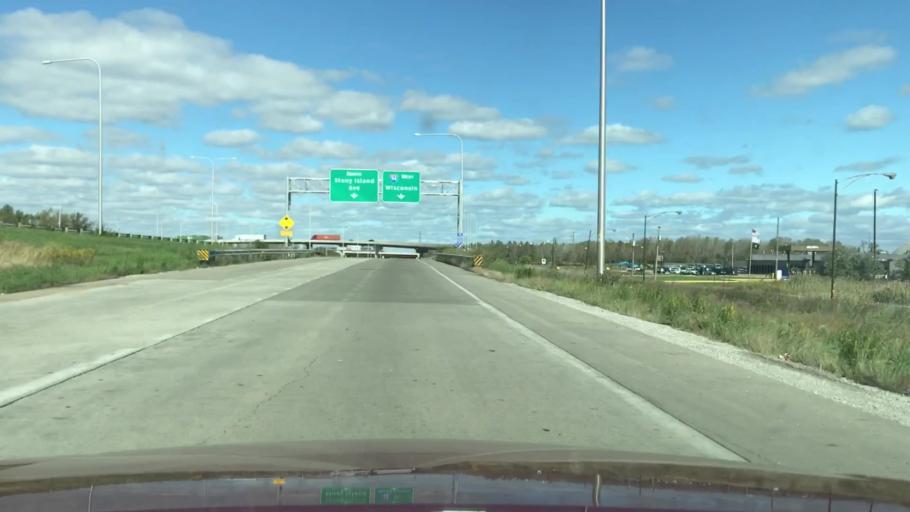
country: US
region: Illinois
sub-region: Cook County
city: Dolton
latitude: 41.7093
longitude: -87.5844
